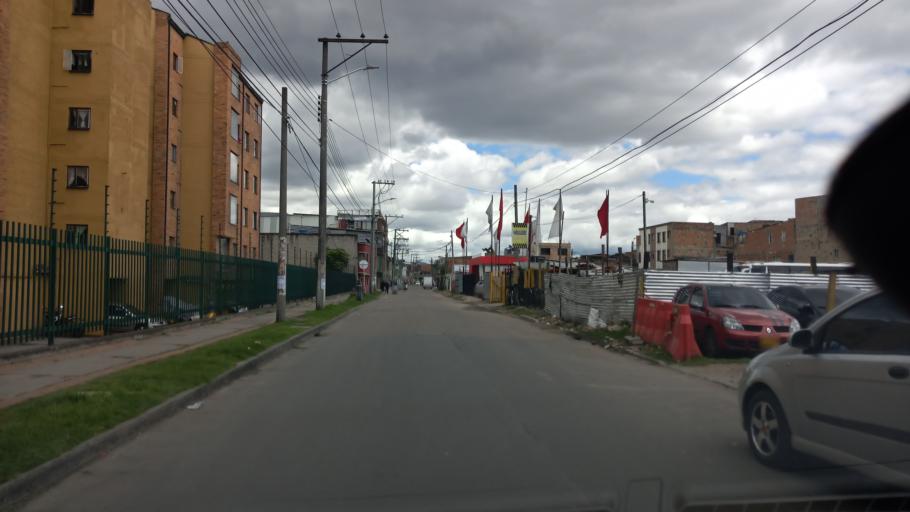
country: CO
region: Cundinamarca
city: Funza
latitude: 4.6682
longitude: -74.1483
